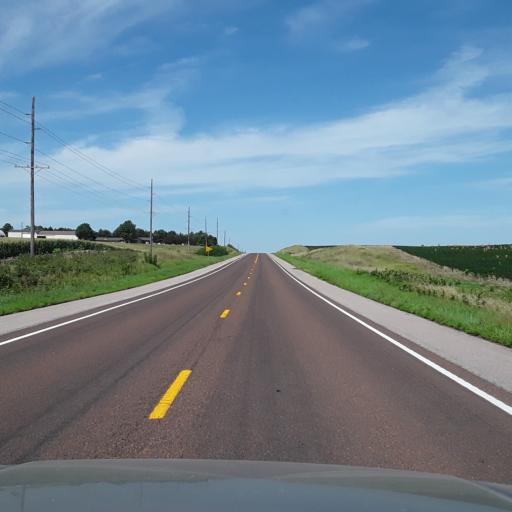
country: US
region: Nebraska
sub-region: Seward County
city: Milford
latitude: 40.8865
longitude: -96.8839
